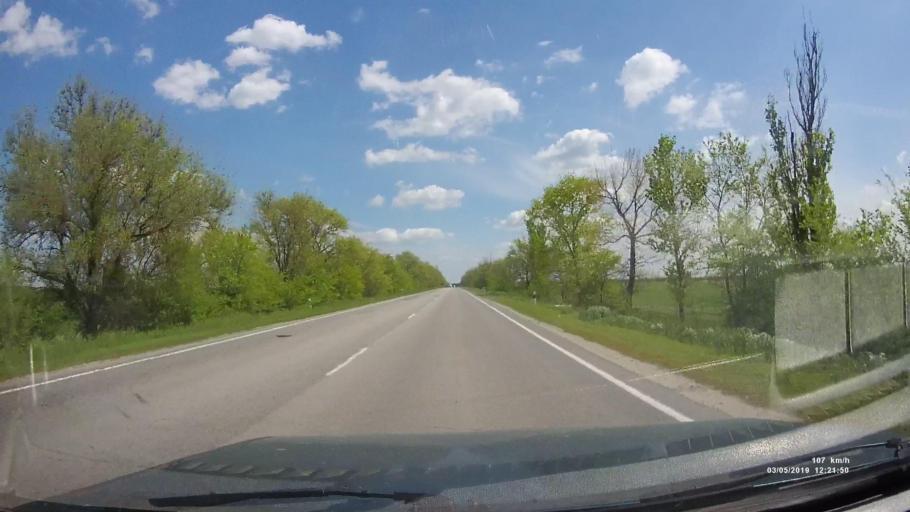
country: RU
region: Rostov
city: Melikhovskaya
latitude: 47.4057
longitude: 40.6474
